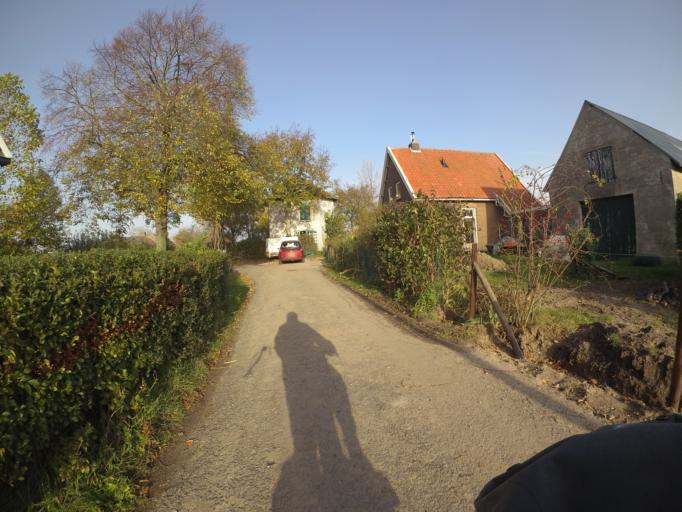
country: NL
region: Gelderland
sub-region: Gemeente Maasdriel
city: Heerewaarden
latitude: 51.8211
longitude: 5.3866
